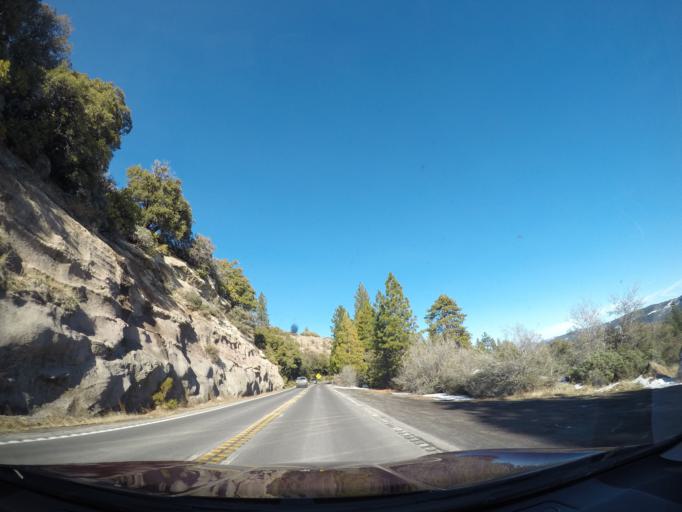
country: US
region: California
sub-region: Tuolumne County
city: Twain Harte
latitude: 38.1415
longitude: -120.0885
